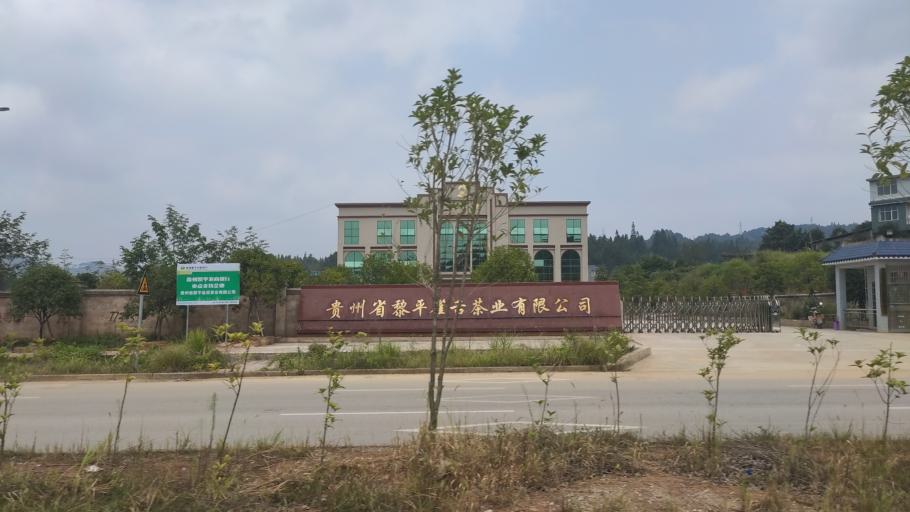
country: CN
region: Guizhou Sheng
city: Zhongchao
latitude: 26.1164
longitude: 109.1924
